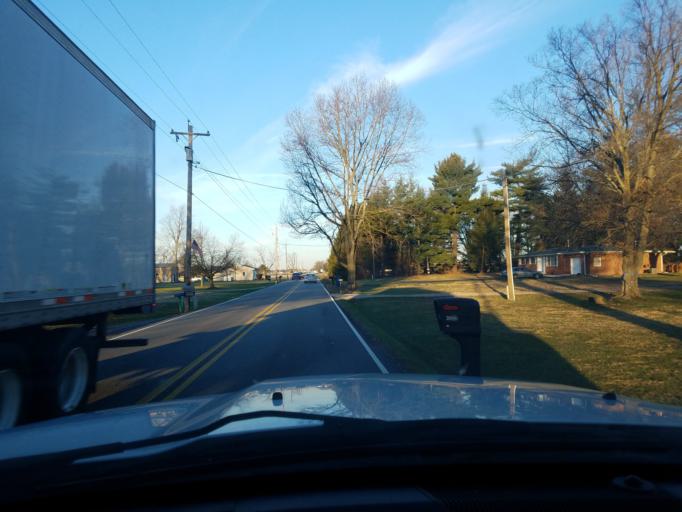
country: US
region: Indiana
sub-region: Johnson County
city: Whiteland
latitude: 39.5506
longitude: -86.0524
